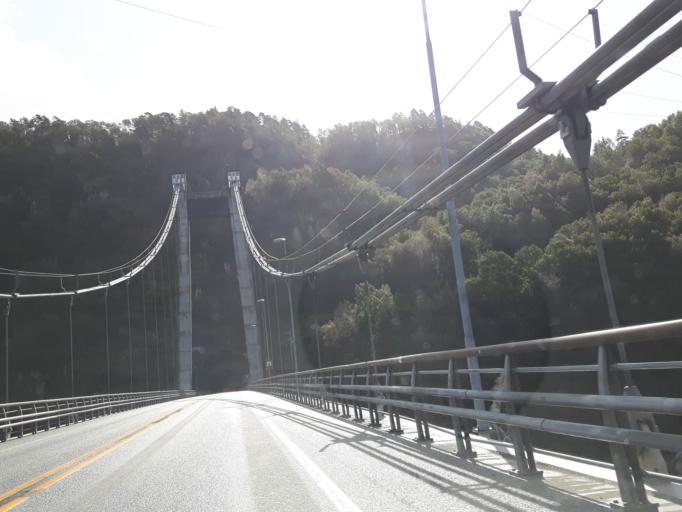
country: NO
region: Vest-Agder
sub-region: Kvinesdal
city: Liknes
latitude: 58.2611
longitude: 6.8456
